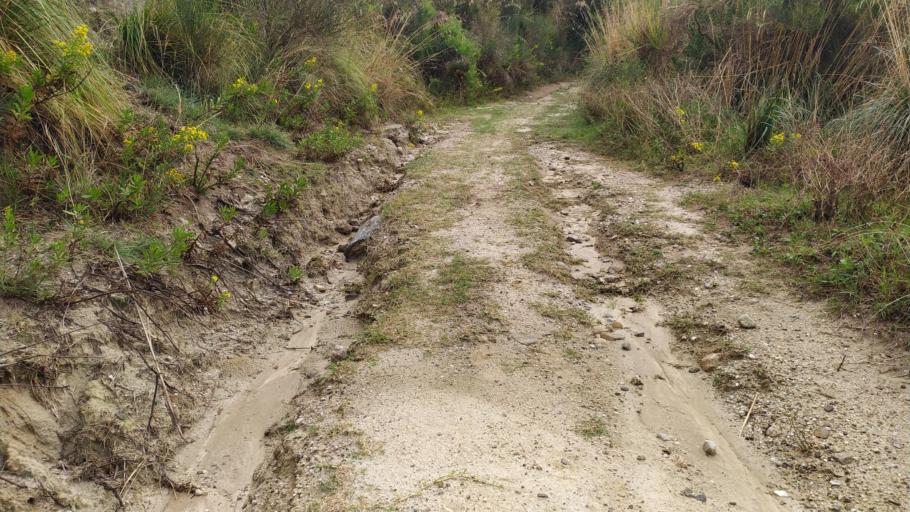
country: IT
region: Sicily
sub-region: Messina
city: Saponara
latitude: 38.2113
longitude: 15.4785
